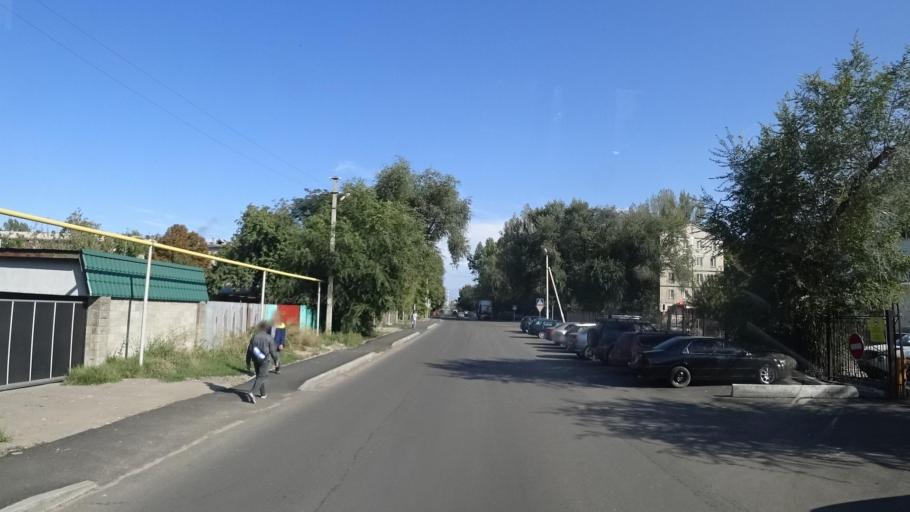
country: KZ
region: Almaty Oblysy
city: Energeticheskiy
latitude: 43.4266
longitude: 77.0213
